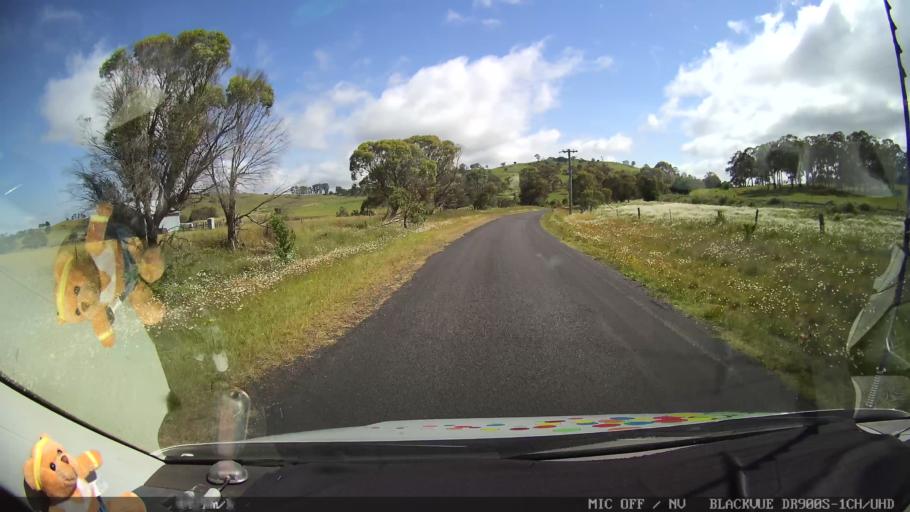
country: AU
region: New South Wales
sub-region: Guyra
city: Guyra
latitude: -30.0136
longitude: 151.6575
